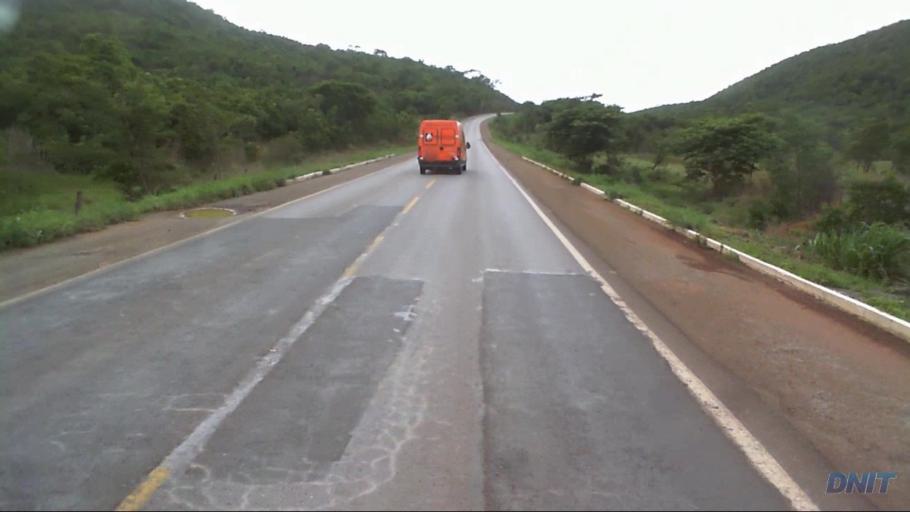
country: BR
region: Goias
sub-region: Barro Alto
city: Barro Alto
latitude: -14.9131
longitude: -48.9554
